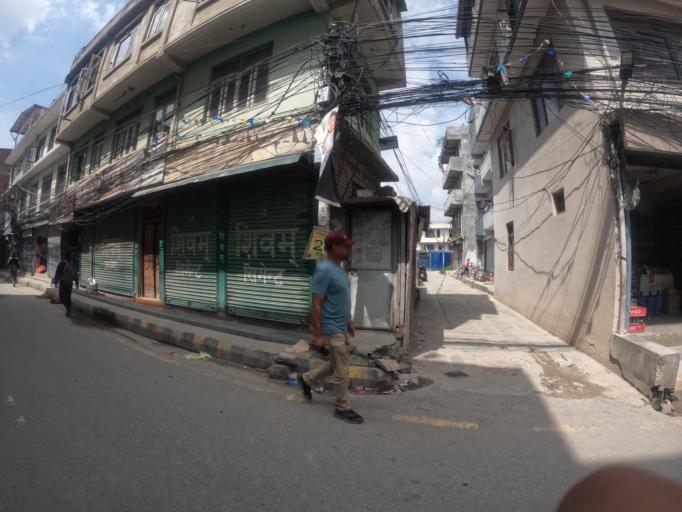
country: NP
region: Central Region
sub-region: Bagmati Zone
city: Patan
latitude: 27.6775
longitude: 85.3619
